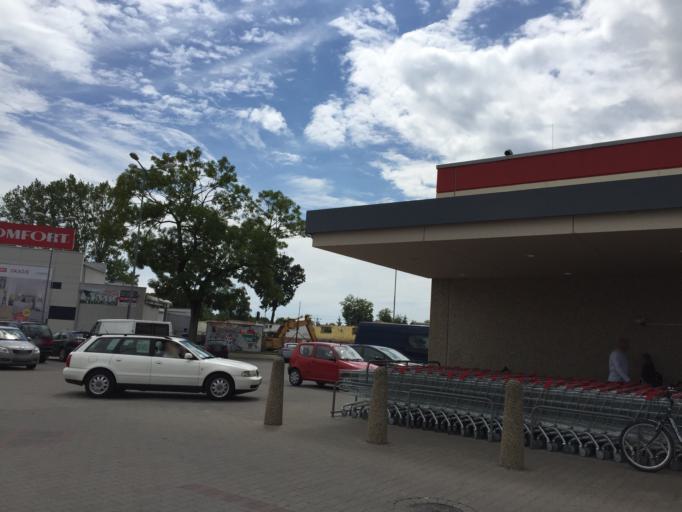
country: PL
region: Podlasie
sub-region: Powiat bielski
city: Bielsk Podlaski
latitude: 52.7692
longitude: 23.1818
